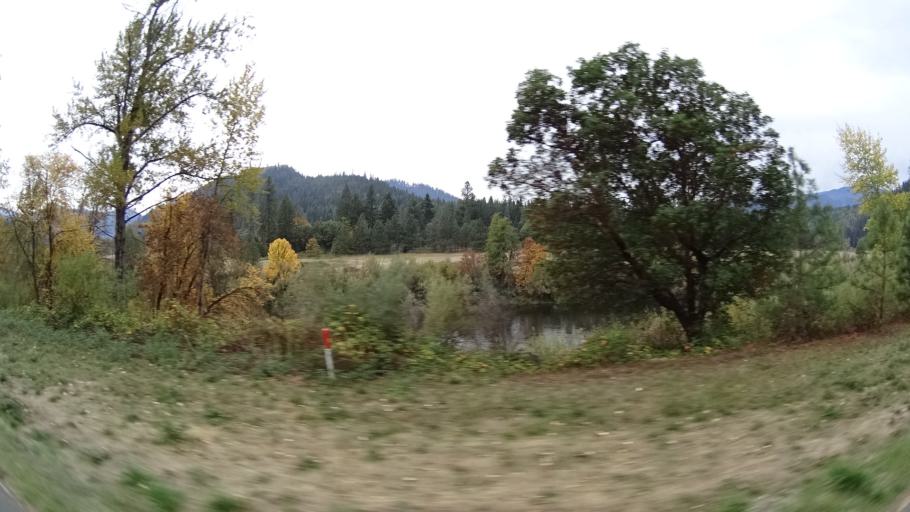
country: US
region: California
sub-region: Siskiyou County
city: Happy Camp
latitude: 41.8099
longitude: -123.3516
